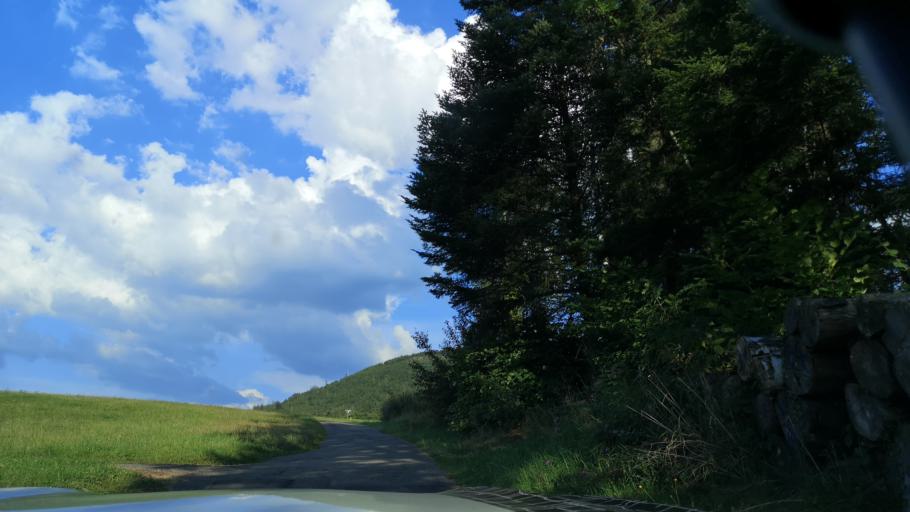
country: DE
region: Baden-Wuerttemberg
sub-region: Karlsruhe Region
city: Bad Herrenalb
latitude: 48.7680
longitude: 8.4382
